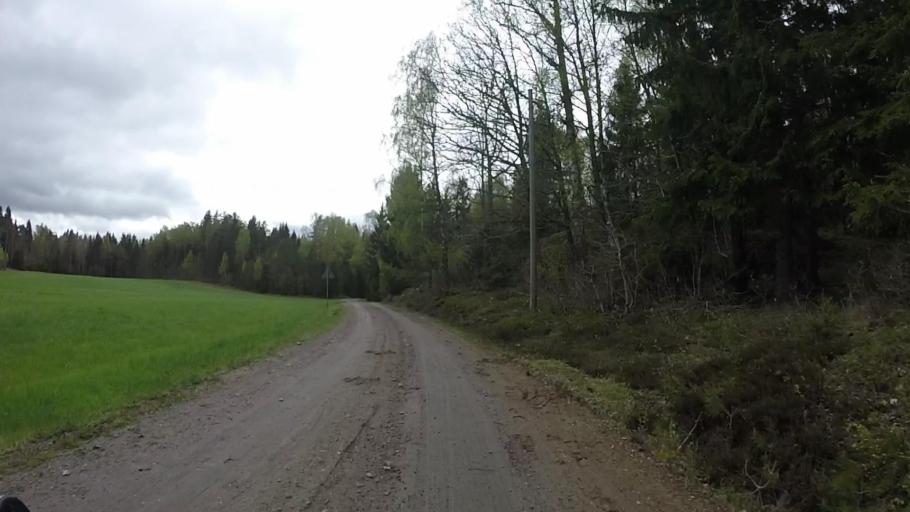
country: SE
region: Vaestra Goetaland
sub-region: Trollhattan
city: Sjuntorp
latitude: 58.2454
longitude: 12.2178
